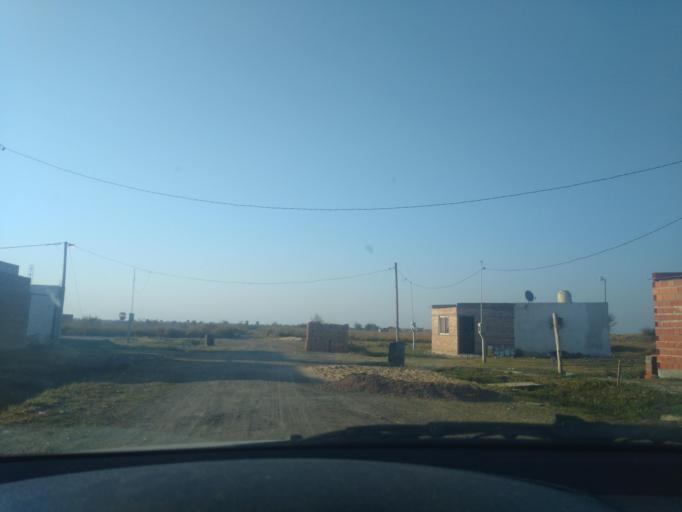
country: AR
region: Chaco
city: Resistencia
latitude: -27.4872
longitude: -59.0160
